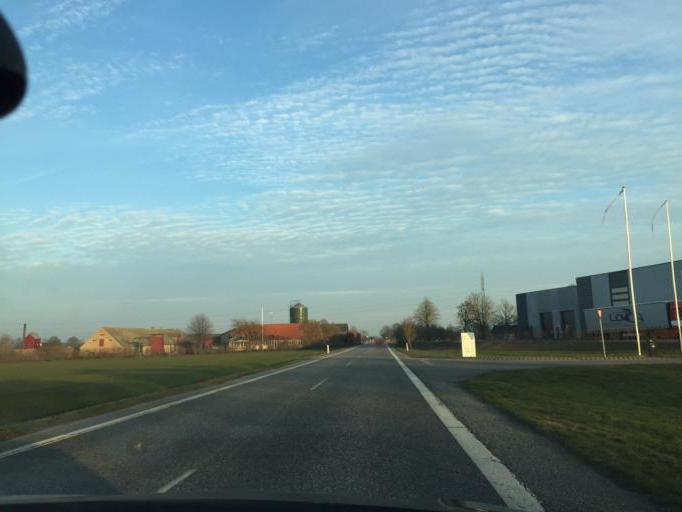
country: DK
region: South Denmark
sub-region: Faaborg-Midtfyn Kommune
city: Arslev
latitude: 55.3342
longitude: 10.5121
